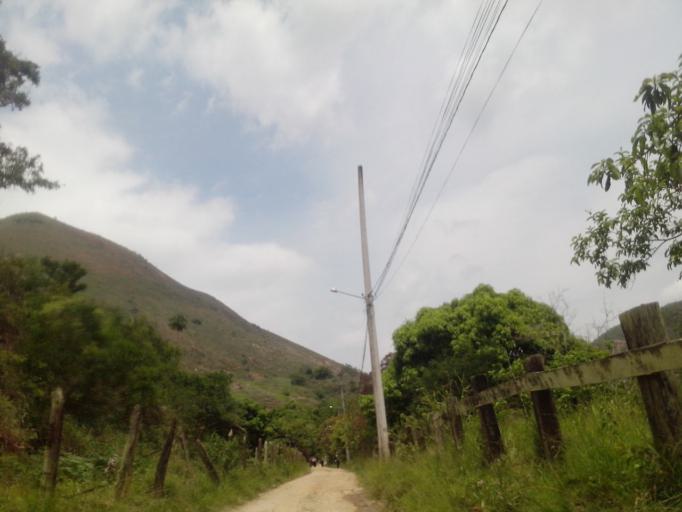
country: BR
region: Rio de Janeiro
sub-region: Miguel Pereira
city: Miguel Pereira
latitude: -22.4911
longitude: -43.4564
